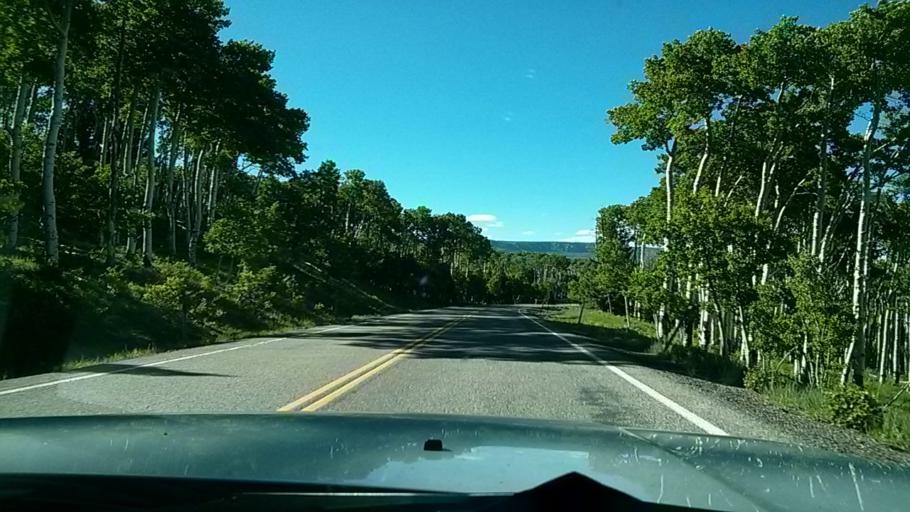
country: US
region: Utah
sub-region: Wayne County
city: Loa
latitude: 38.0621
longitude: -111.3284
